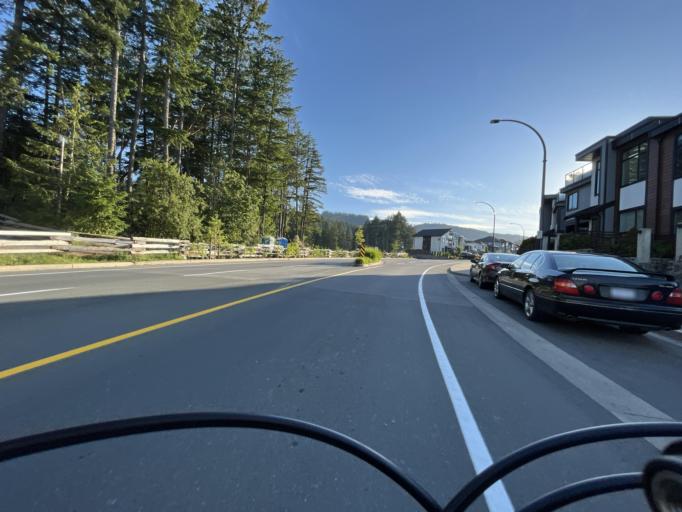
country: CA
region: British Columbia
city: Langford
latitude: 48.4441
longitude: -123.5394
